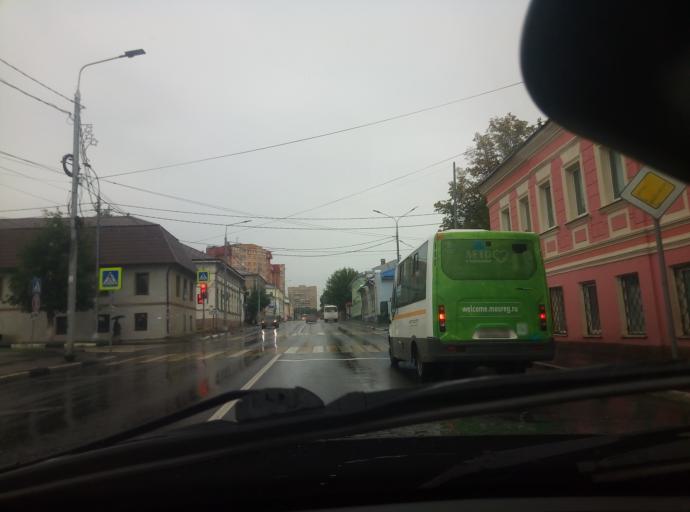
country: RU
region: Moskovskaya
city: Serpukhov
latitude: 54.9155
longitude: 37.4170
